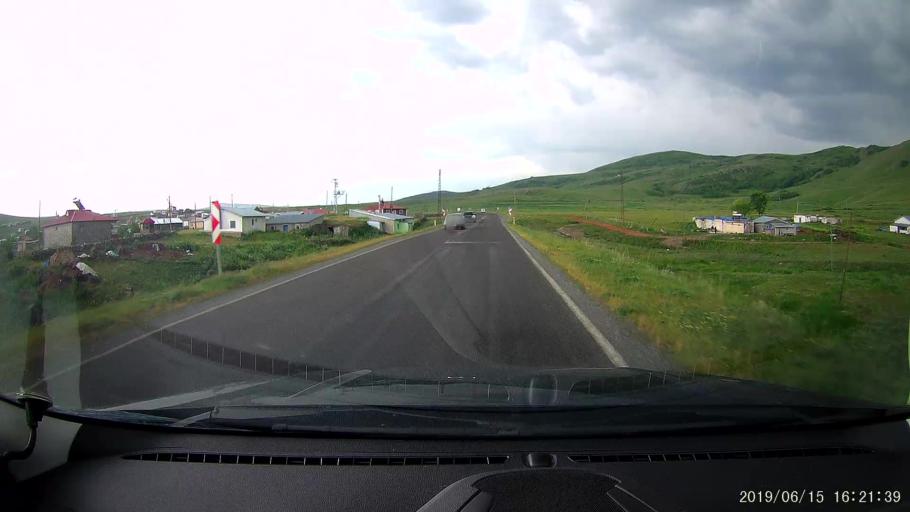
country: TR
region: Ardahan
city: Hanak
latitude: 41.1970
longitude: 42.8468
